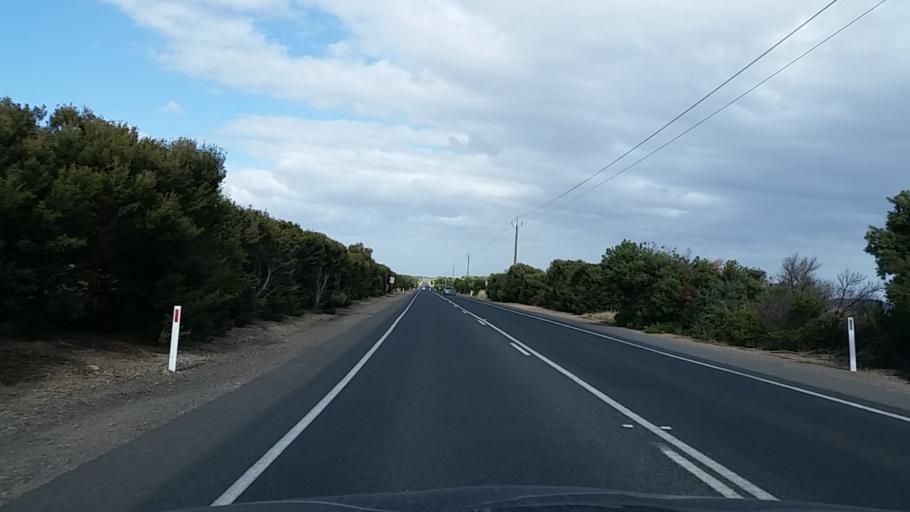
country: AU
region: South Australia
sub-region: Alexandrina
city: Port Elliot
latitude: -35.5095
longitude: 138.7238
